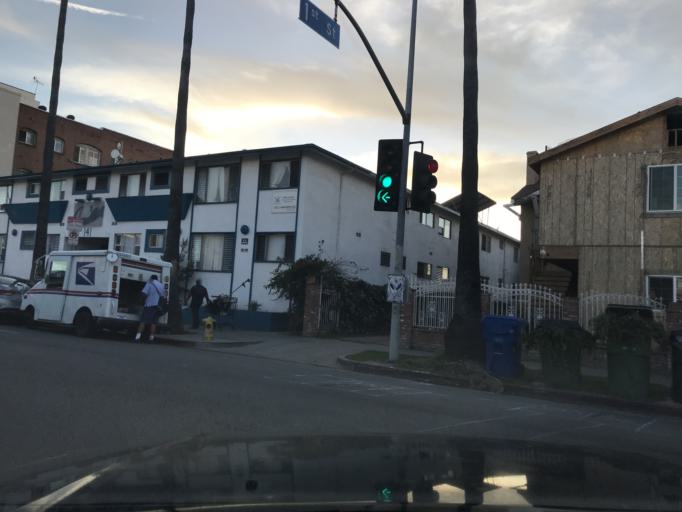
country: US
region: California
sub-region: Los Angeles County
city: Silver Lake
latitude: 34.0728
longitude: -118.3004
